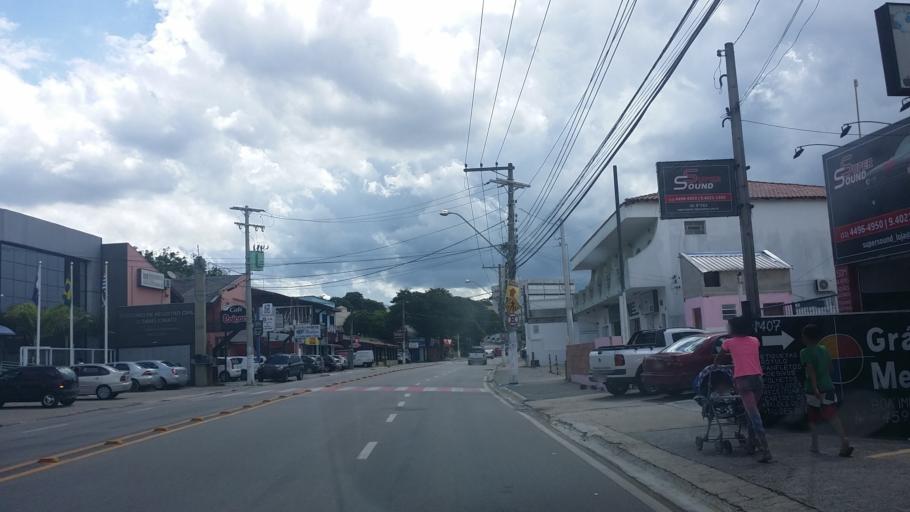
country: BR
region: Sao Paulo
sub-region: Itupeva
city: Itupeva
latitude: -23.1555
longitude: -47.0542
